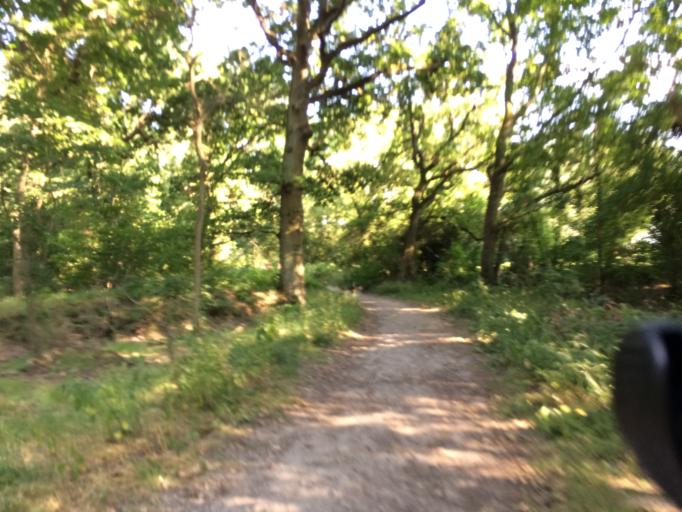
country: FR
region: Ile-de-France
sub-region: Departement de l'Essonne
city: Soisy-sur-Seine
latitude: 48.6526
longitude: 2.4681
